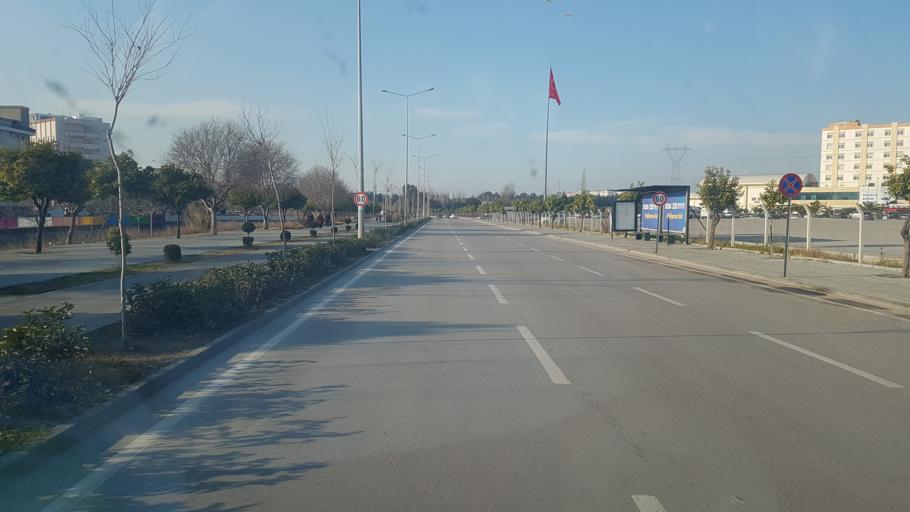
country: TR
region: Adana
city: Adana
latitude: 37.0088
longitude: 35.3537
